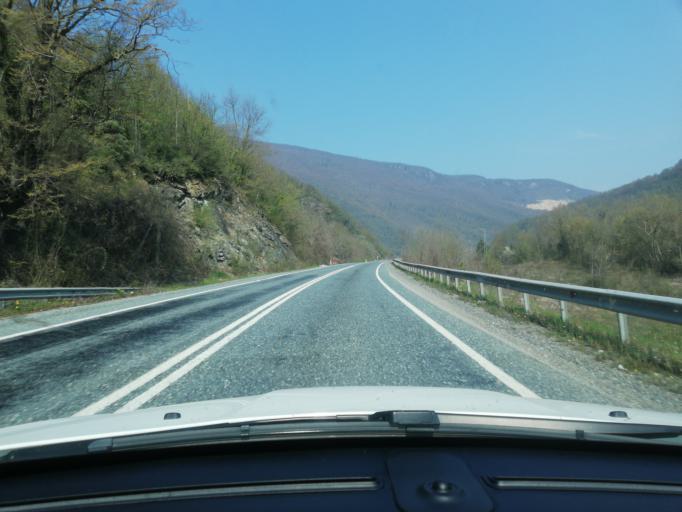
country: TR
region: Zonguldak
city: Gokcebey
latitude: 41.2574
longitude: 32.1574
